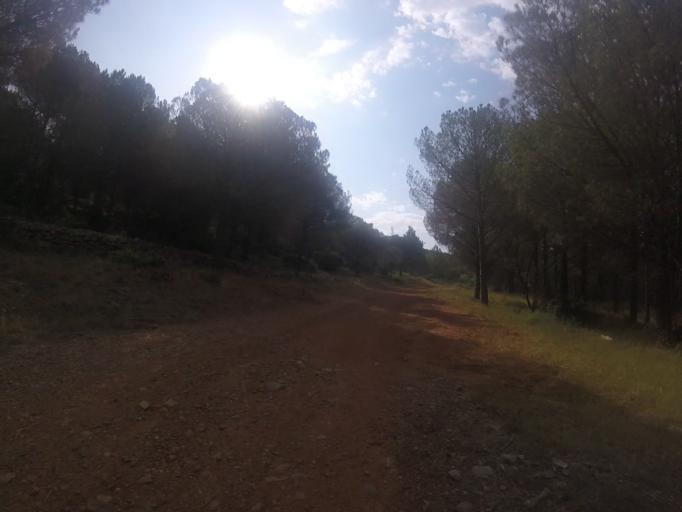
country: ES
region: Valencia
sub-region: Provincia de Castello
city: Cervera del Maestre
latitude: 40.3972
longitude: 0.2066
